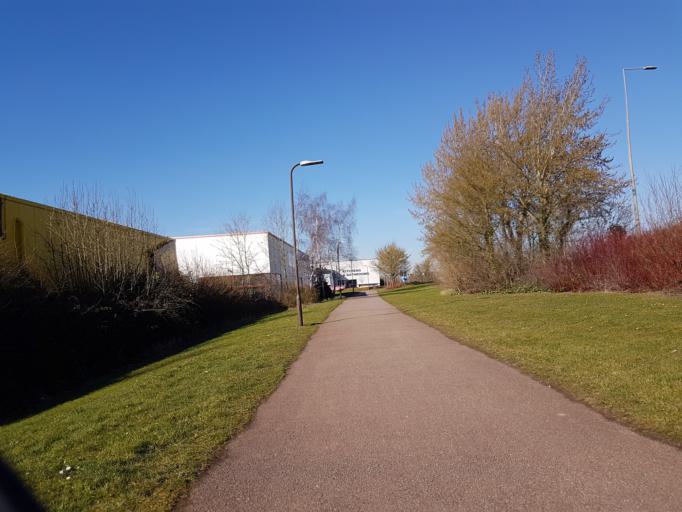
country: GB
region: England
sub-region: Milton Keynes
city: Milton Keynes
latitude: 52.0271
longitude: -0.7609
